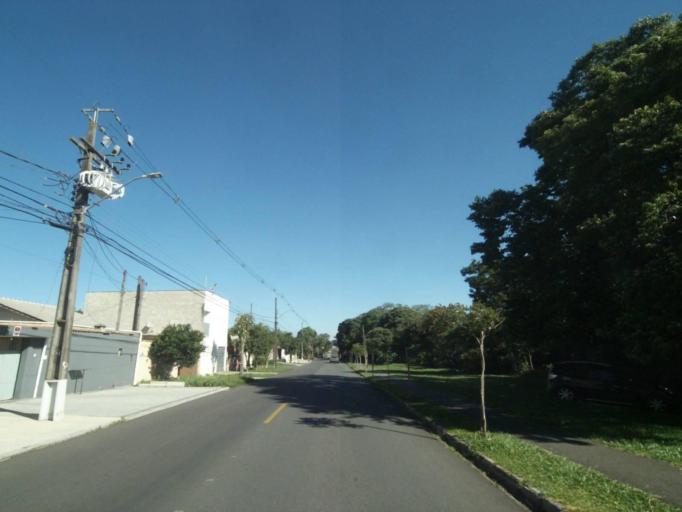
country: BR
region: Parana
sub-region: Curitiba
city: Curitiba
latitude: -25.4562
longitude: -49.3551
